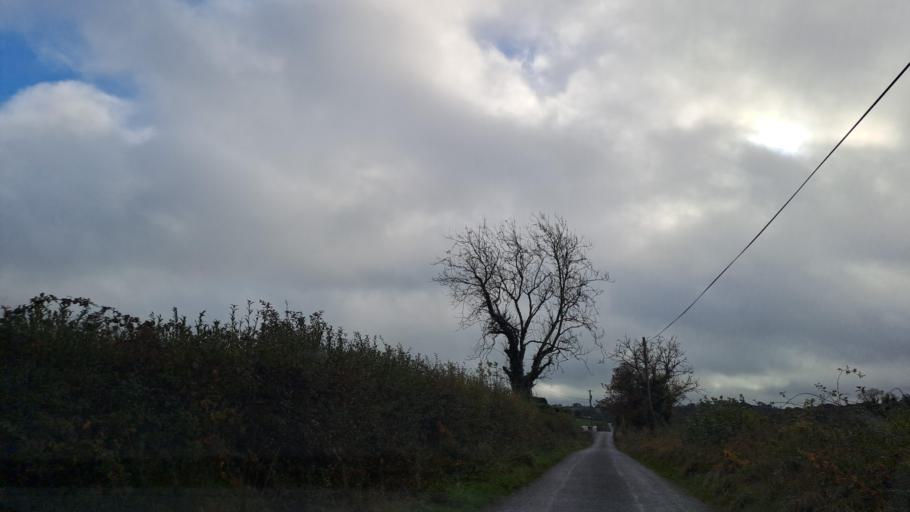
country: IE
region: Ulster
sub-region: An Cabhan
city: Bailieborough
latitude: 53.9816
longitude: -7.0036
